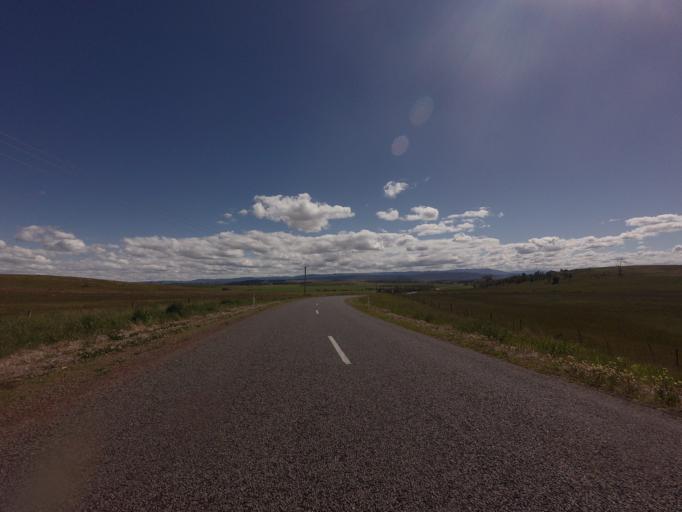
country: AU
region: Tasmania
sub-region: Northern Midlands
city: Evandale
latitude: -41.9393
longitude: 147.5681
